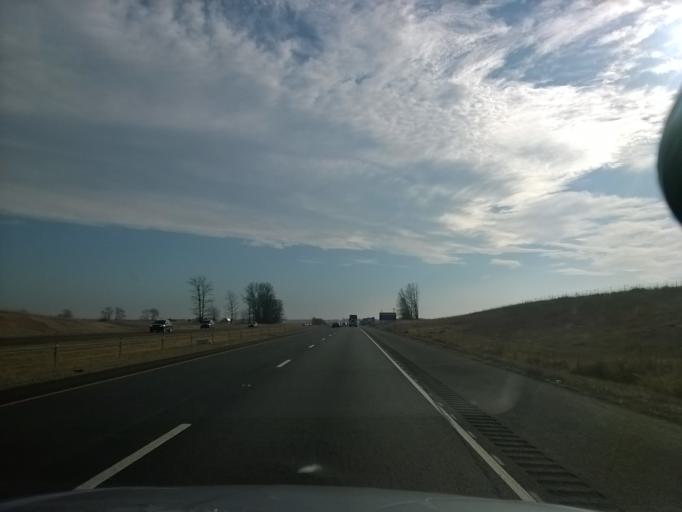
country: US
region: Indiana
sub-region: Johnson County
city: Edinburgh
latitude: 39.3391
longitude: -85.9422
